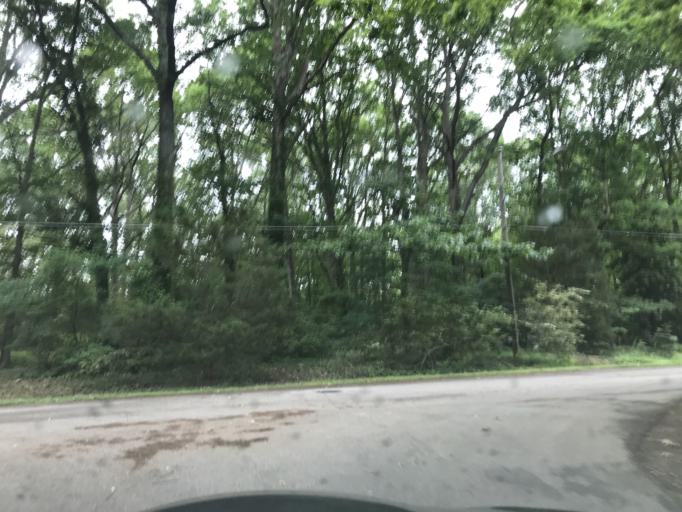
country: US
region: North Carolina
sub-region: Wake County
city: Raleigh
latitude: 35.8587
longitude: -78.5890
